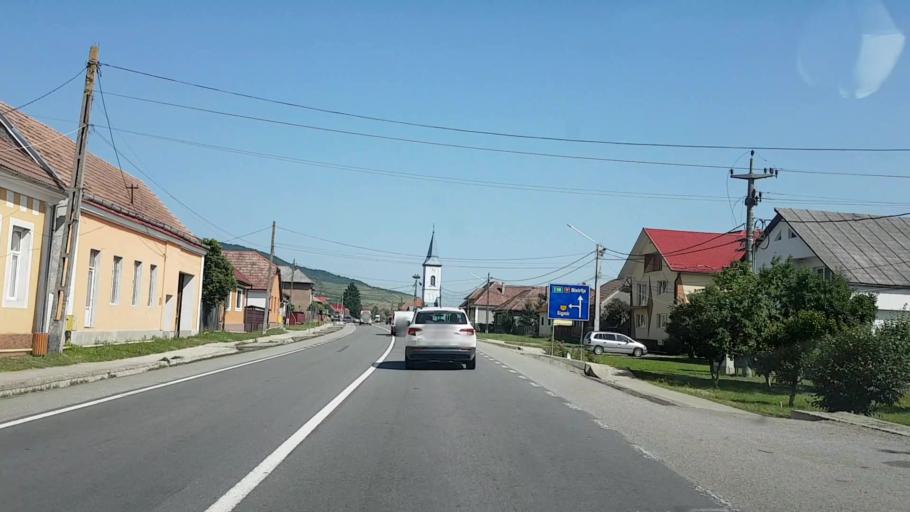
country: RO
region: Bistrita-Nasaud
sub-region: Comuna Sieu-Magherus
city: Sieu-Magherus
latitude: 47.0904
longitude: 24.3743
